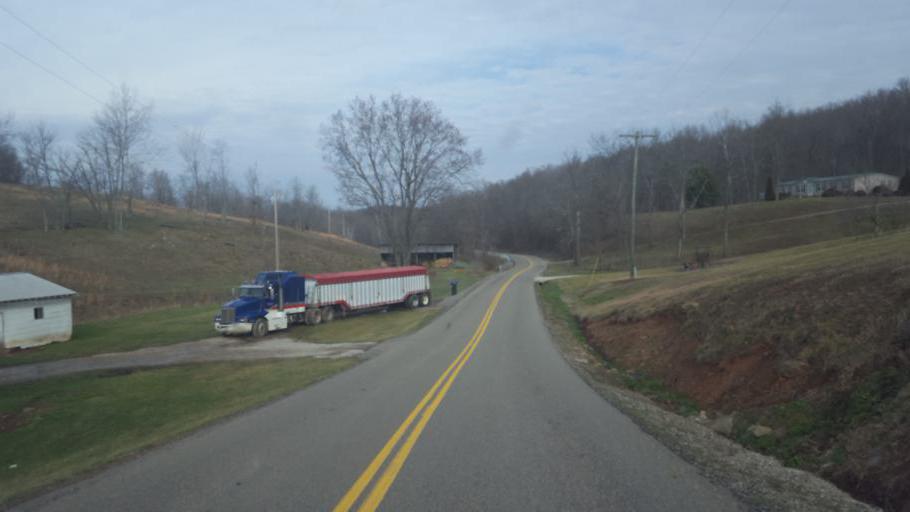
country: US
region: Ohio
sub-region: Gallia County
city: Gallipolis
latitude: 38.7152
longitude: -82.3451
